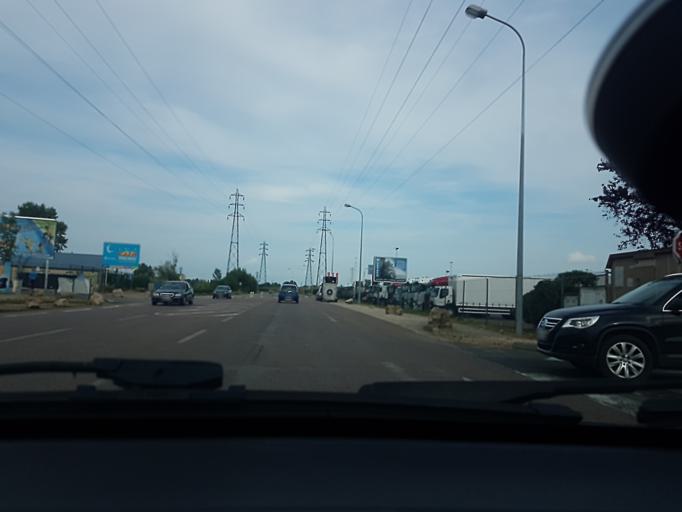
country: FR
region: Bourgogne
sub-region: Departement de Saone-et-Loire
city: Chalon-sur-Saone
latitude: 46.7725
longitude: 4.8682
